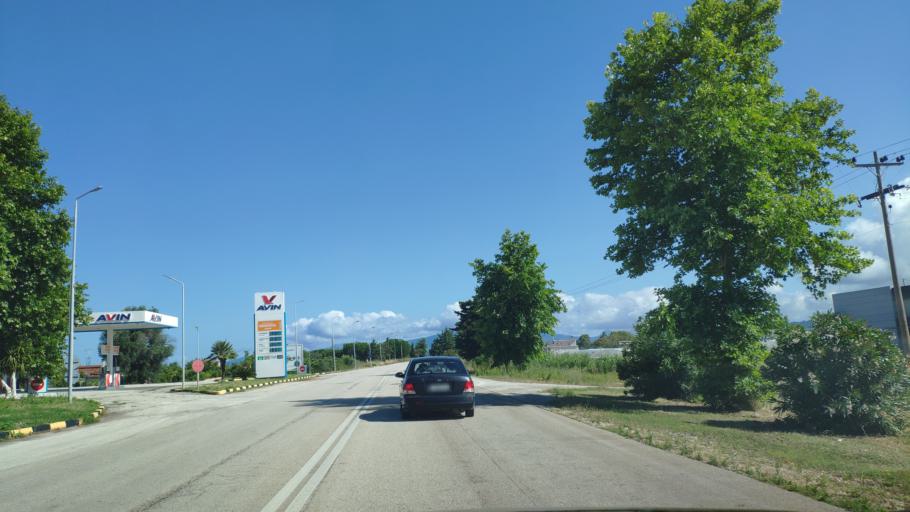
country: GR
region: Epirus
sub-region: Nomos Prevezis
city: Preveza
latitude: 38.9835
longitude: 20.7151
